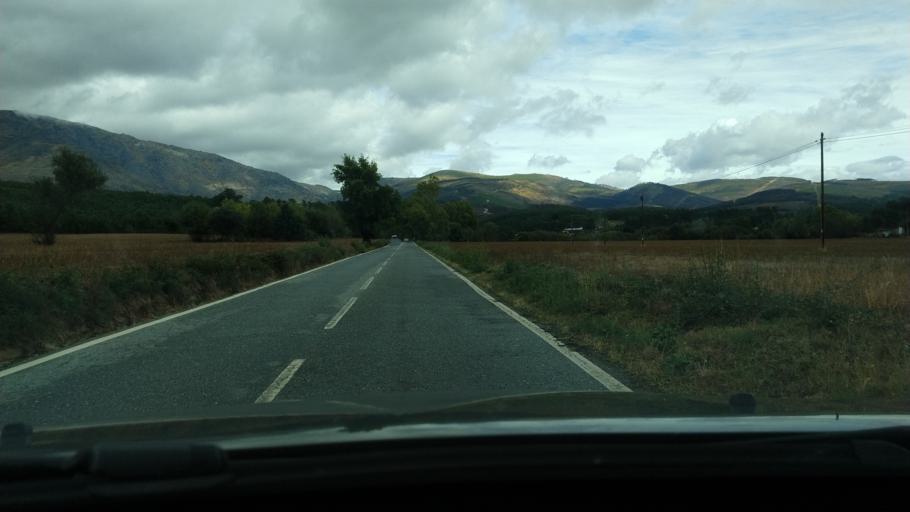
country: PT
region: Castelo Branco
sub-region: Covilha
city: Covilha
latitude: 40.2338
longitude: -7.6014
